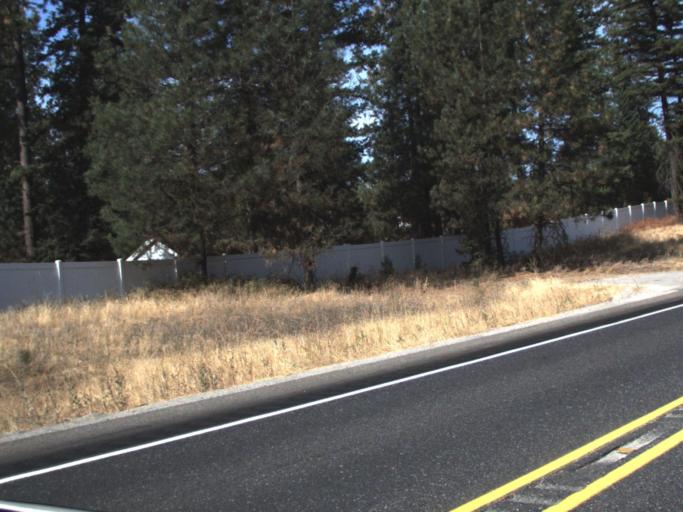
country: US
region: Washington
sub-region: Spokane County
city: Deer Park
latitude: 48.0519
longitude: -117.6138
